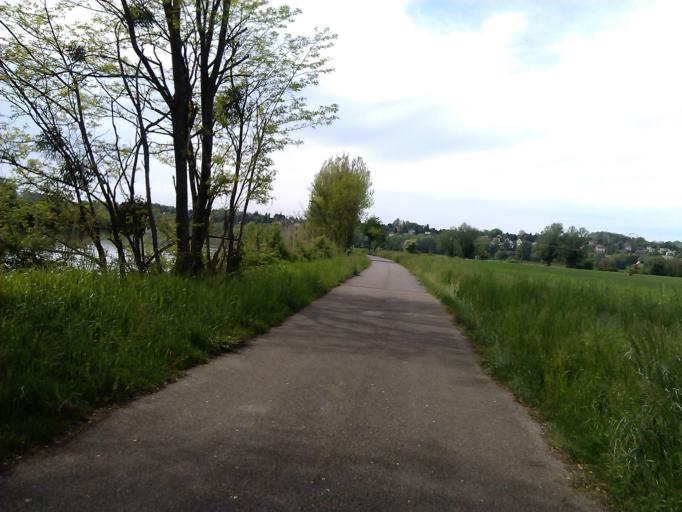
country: FR
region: Franche-Comte
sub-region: Departement du Doubs
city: Saint-Vit
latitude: 47.1709
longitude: 5.8097
